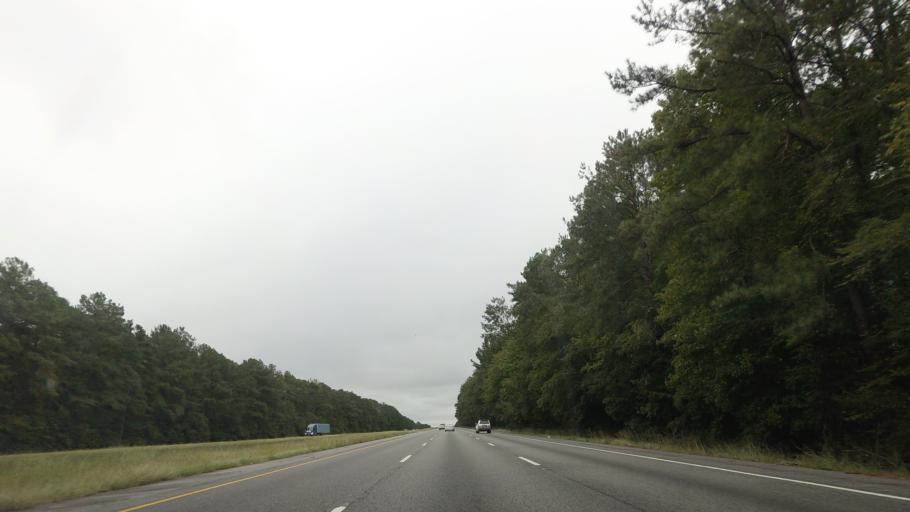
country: US
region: Georgia
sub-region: Houston County
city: Perry
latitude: 32.3639
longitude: -83.7687
